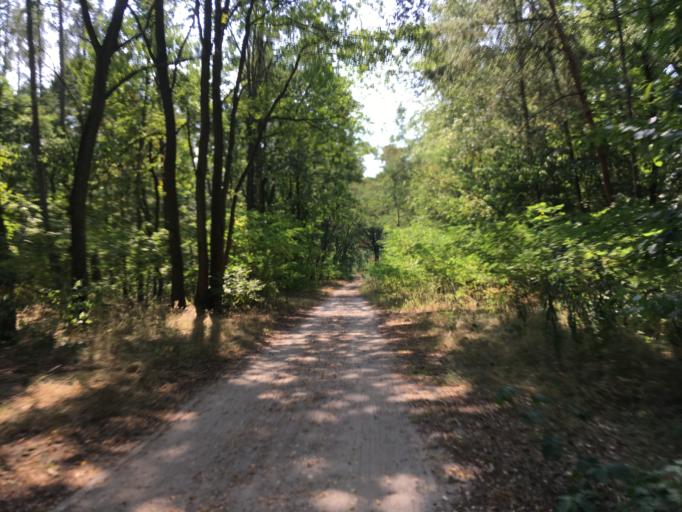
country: DE
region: Berlin
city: Friedrichshagen
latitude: 52.4604
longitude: 13.6040
